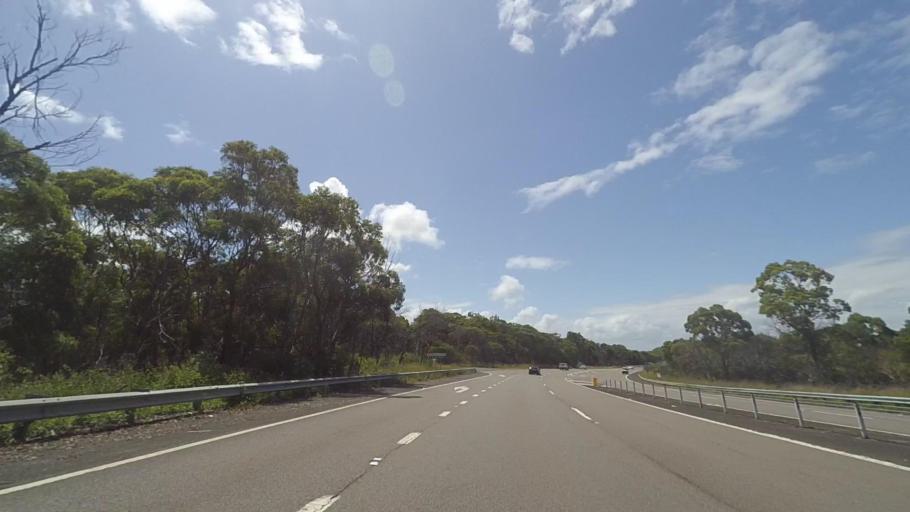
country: AU
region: New South Wales
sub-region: Wyong Shire
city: Kingfisher Shores
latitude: -33.1439
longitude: 151.6109
